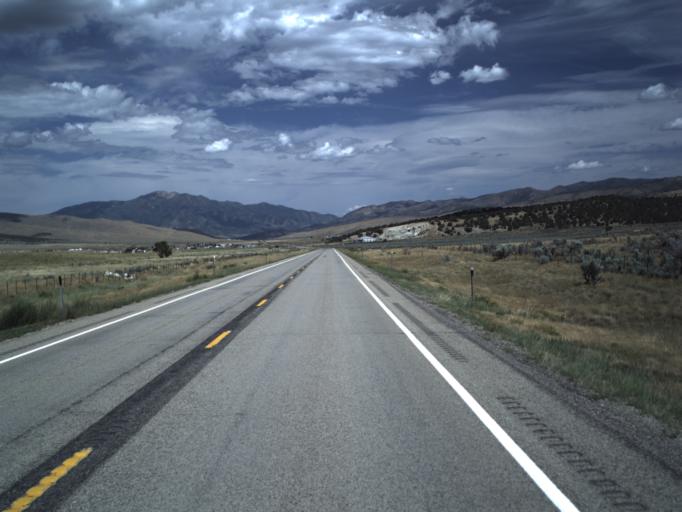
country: US
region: Utah
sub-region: Sanpete County
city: Fairview
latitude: 39.7496
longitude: -111.4784
